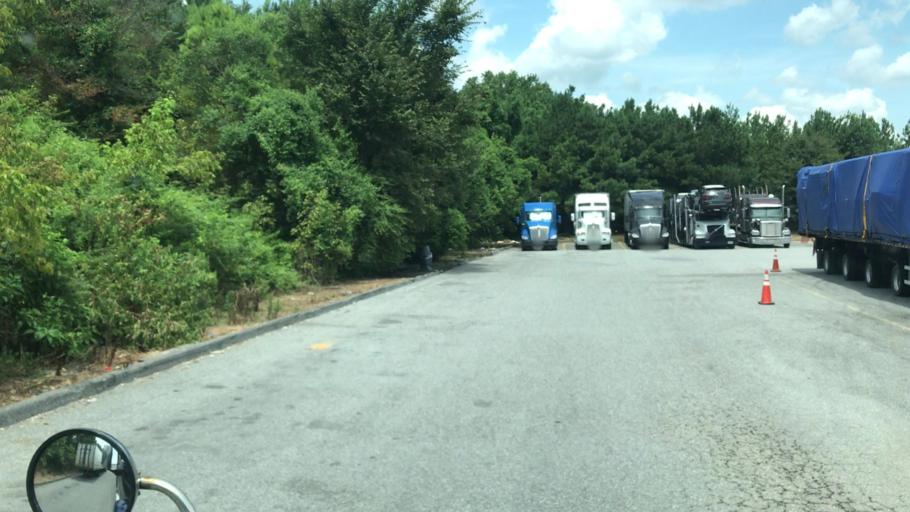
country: US
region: Georgia
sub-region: Bartow County
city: Cartersville
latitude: 34.2753
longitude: -84.8094
